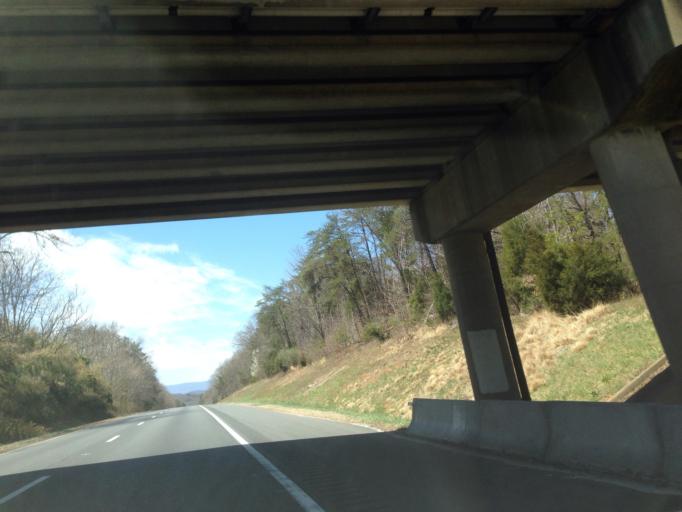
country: US
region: Virginia
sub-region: Albemarle County
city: Crozet
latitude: 38.0333
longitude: -78.6365
